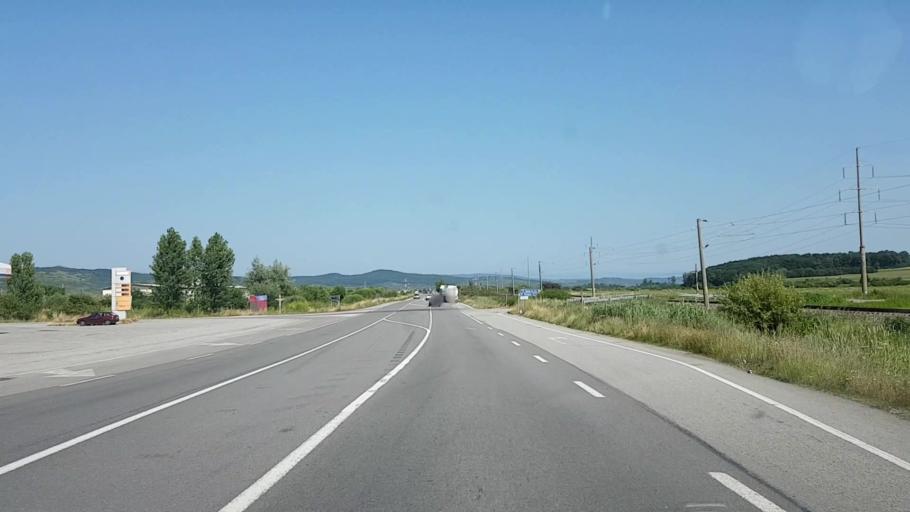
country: RO
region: Bistrita-Nasaud
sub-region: Comuna Sintereag
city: Cociu
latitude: 47.1825
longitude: 24.2378
